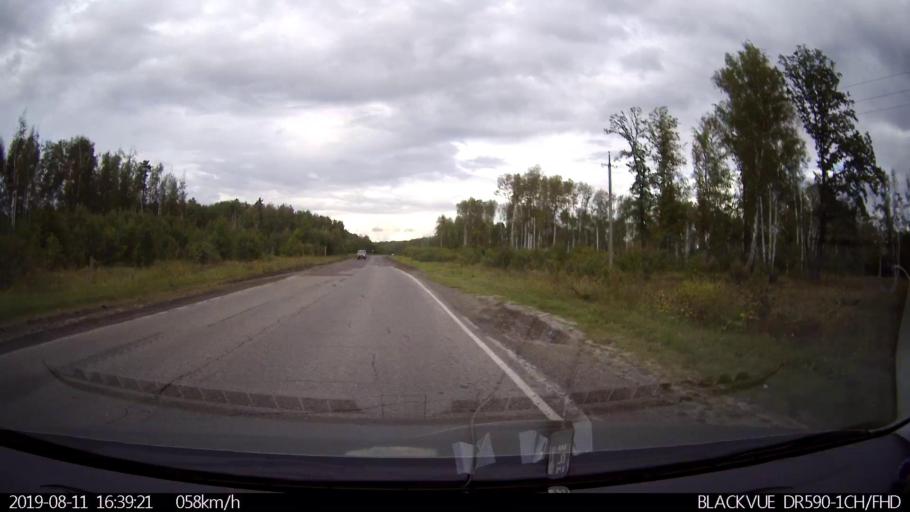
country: RU
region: Ulyanovsk
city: Mayna
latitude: 54.1394
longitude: 47.6364
